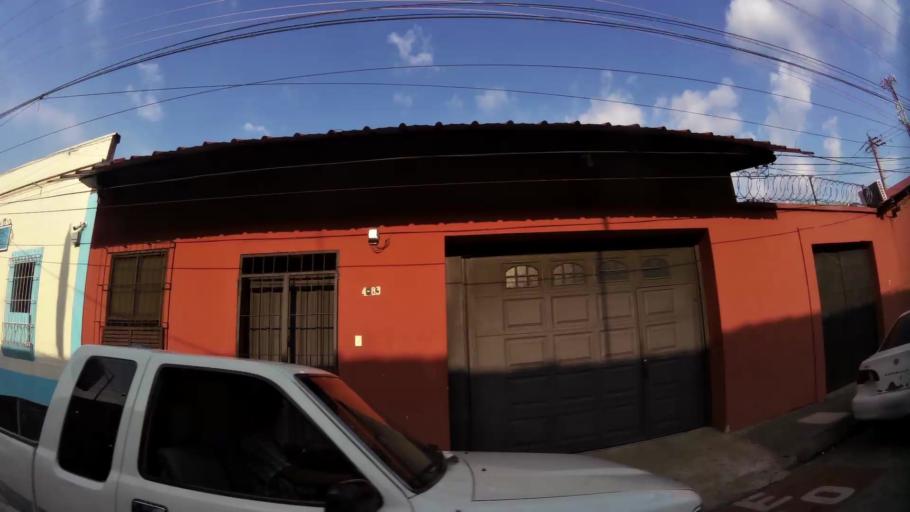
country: GT
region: Retalhuleu
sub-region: Municipio de Retalhuleu
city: Retalhuleu
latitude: 14.5377
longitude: -91.6772
